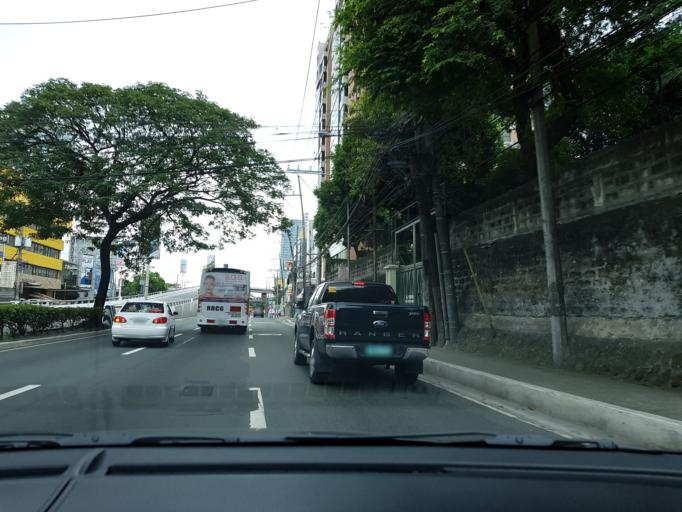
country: PH
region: Metro Manila
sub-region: Pasig
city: Pasig City
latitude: 14.5953
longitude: 121.0557
